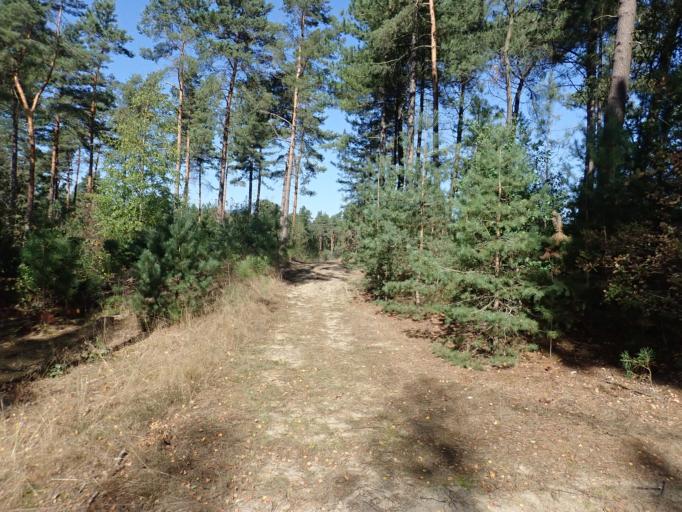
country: BE
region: Flanders
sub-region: Provincie Antwerpen
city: Kasterlee
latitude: 51.2146
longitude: 4.8970
